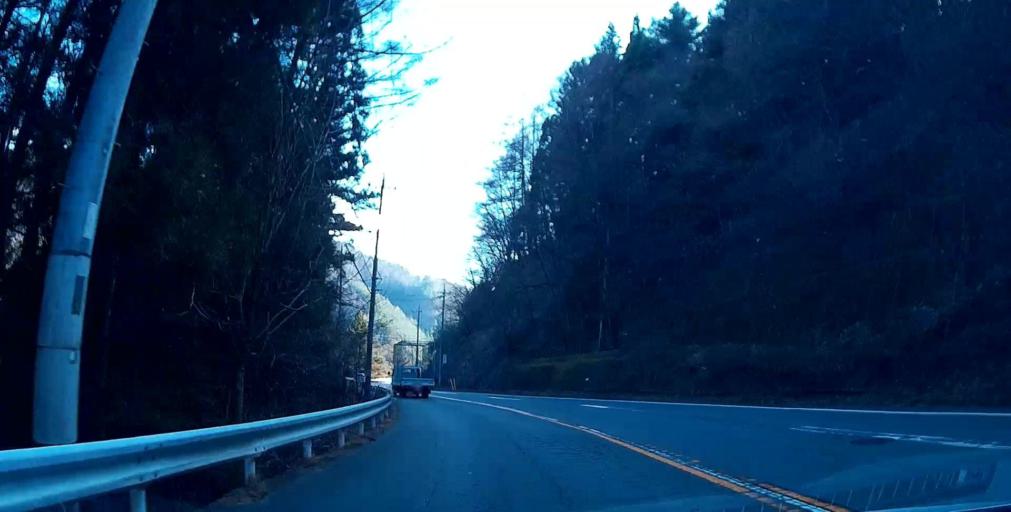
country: JP
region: Yamanashi
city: Fujikawaguchiko
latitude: 35.5431
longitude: 138.7704
